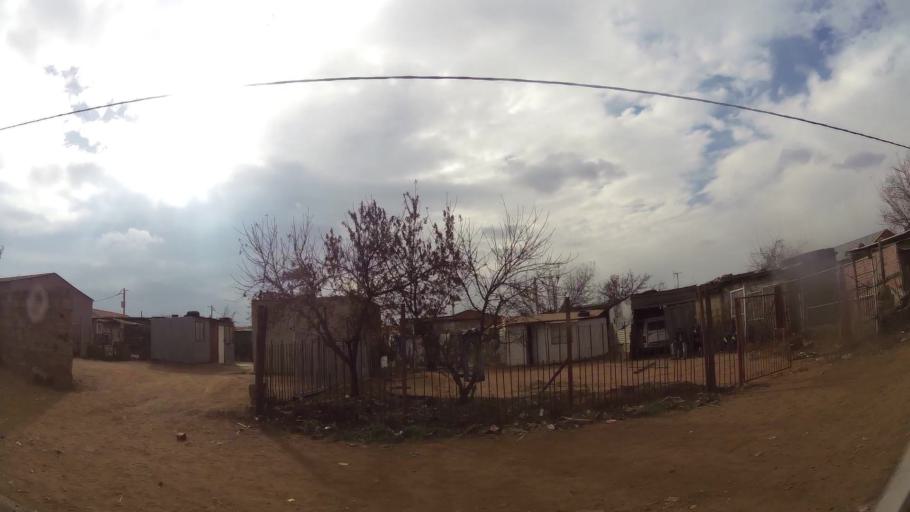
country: ZA
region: Gauteng
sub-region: Ekurhuleni Metropolitan Municipality
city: Germiston
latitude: -26.4018
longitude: 28.1600
